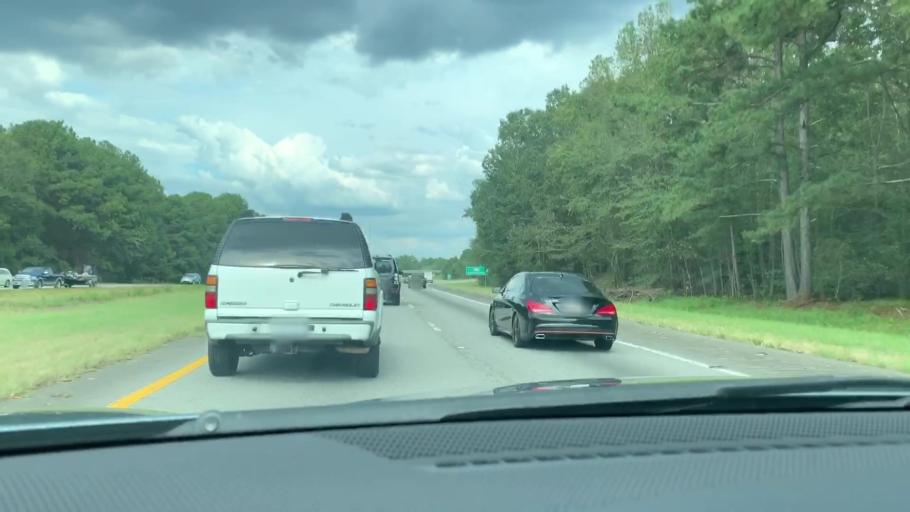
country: US
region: South Carolina
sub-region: Jasper County
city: Ridgeland
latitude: 32.5749
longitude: -80.9353
